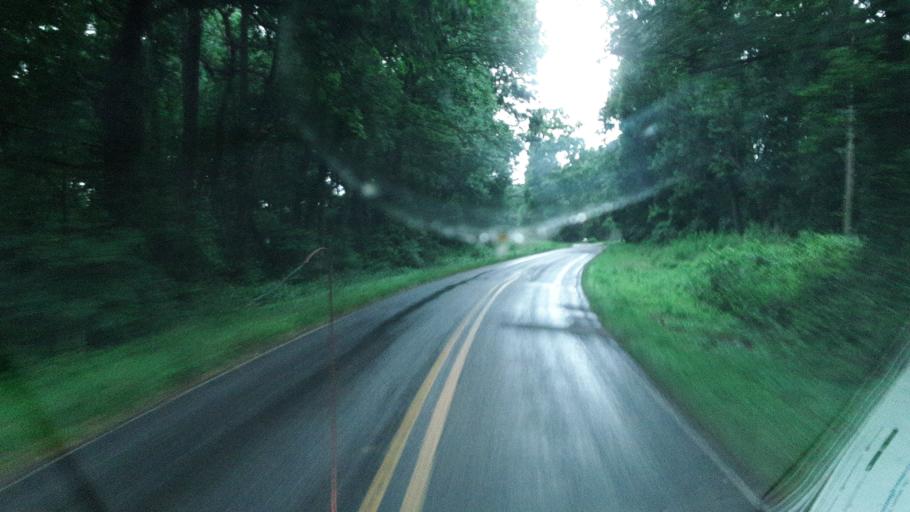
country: US
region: North Carolina
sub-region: Yadkin County
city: Jonesville
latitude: 36.1063
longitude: -80.8804
